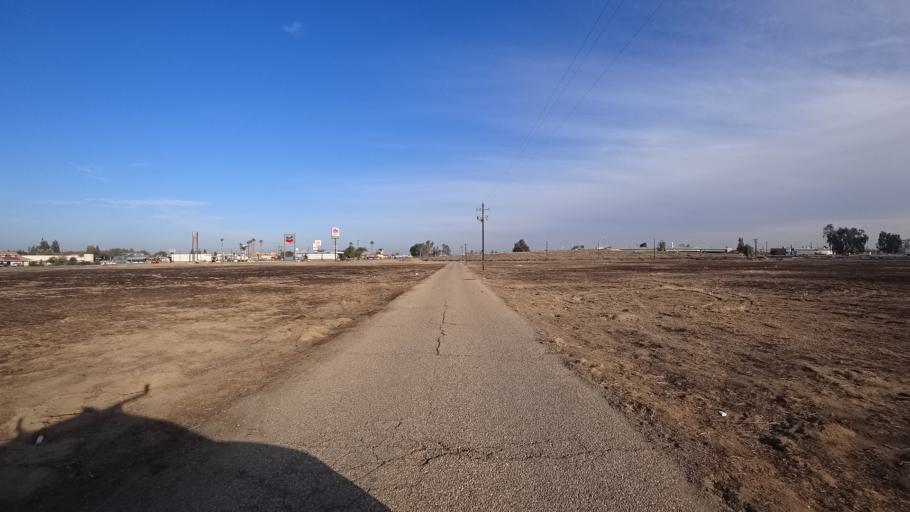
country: US
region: California
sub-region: Kern County
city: Oildale
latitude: 35.4099
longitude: -119.0567
